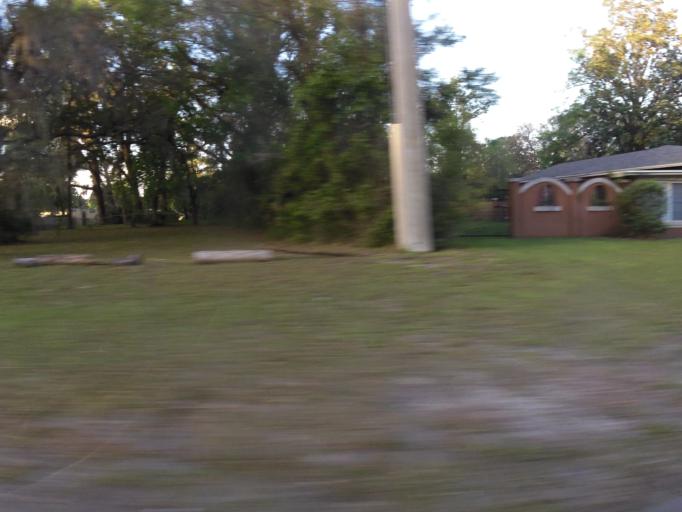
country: US
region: Florida
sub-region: Duval County
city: Jacksonville
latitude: 30.2843
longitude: -81.5754
